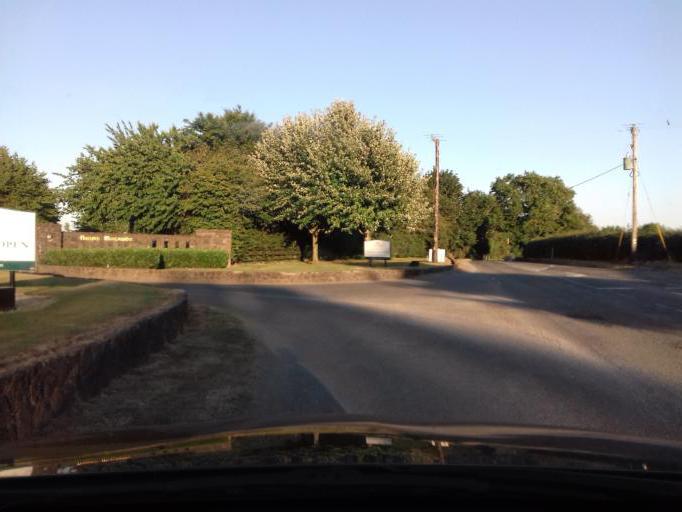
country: IE
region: Leinster
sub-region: Dublin City
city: Finglas
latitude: 53.4494
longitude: -6.3076
